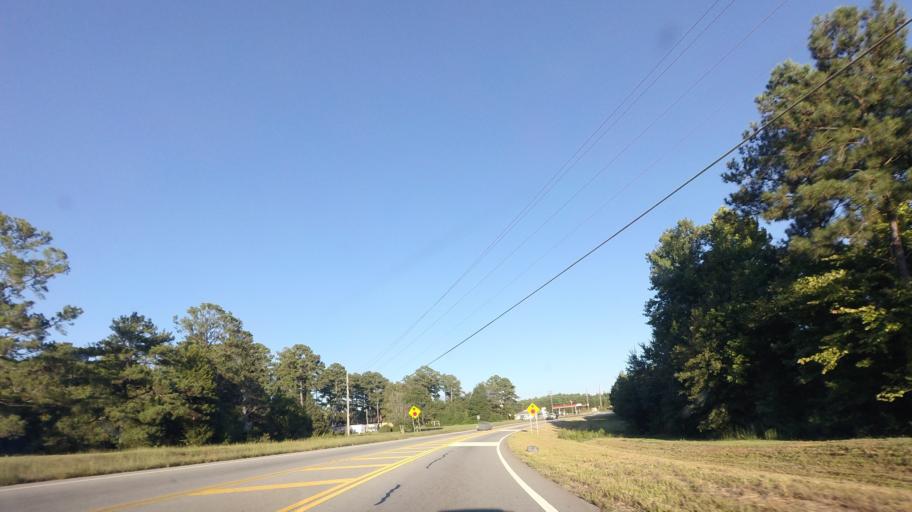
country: US
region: Georgia
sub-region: Spalding County
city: East Griffin
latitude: 33.2932
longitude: -84.1926
